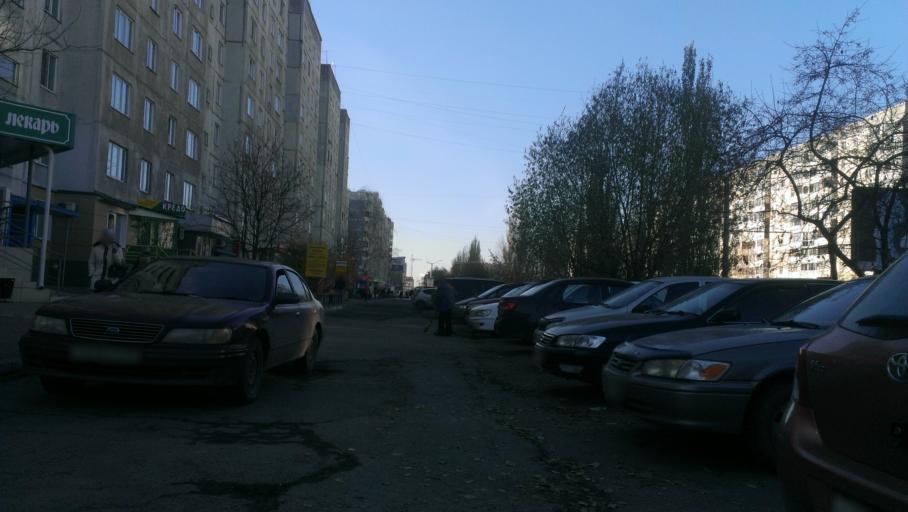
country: RU
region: Altai Krai
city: Novosilikatnyy
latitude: 53.3352
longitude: 83.6754
